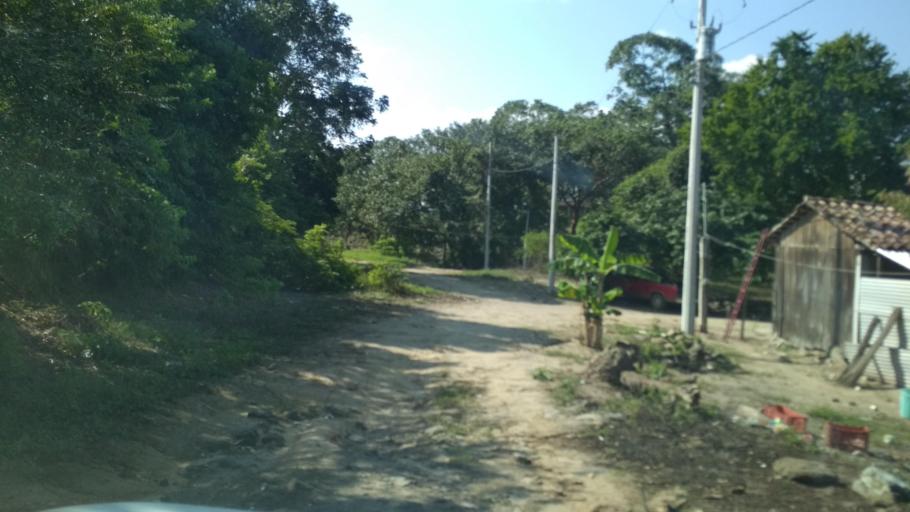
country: MX
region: Puebla
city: San Jose Acateno
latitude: 20.1887
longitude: -97.1554
